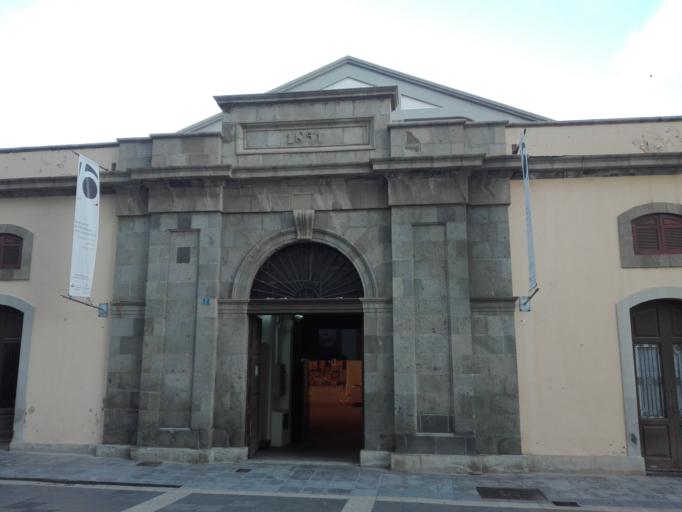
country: ES
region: Canary Islands
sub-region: Provincia de Santa Cruz de Tenerife
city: Santa Cruz de Tenerife
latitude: 28.4657
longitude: -16.2512
